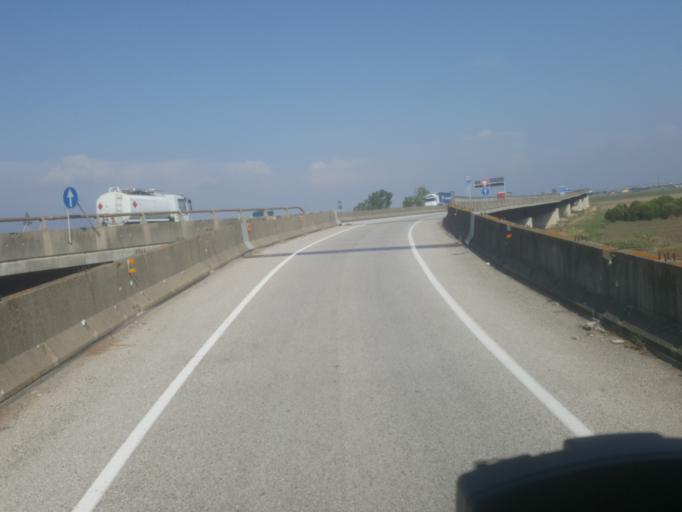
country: IT
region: Tuscany
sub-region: Provincia di Livorno
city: Guasticce
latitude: 43.6094
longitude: 10.4085
